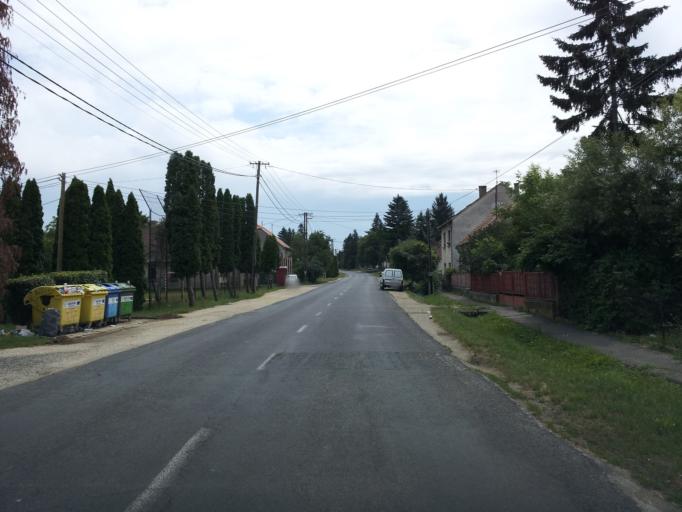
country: HU
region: Zala
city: Zalaszentgrot
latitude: 47.0125
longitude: 16.9691
